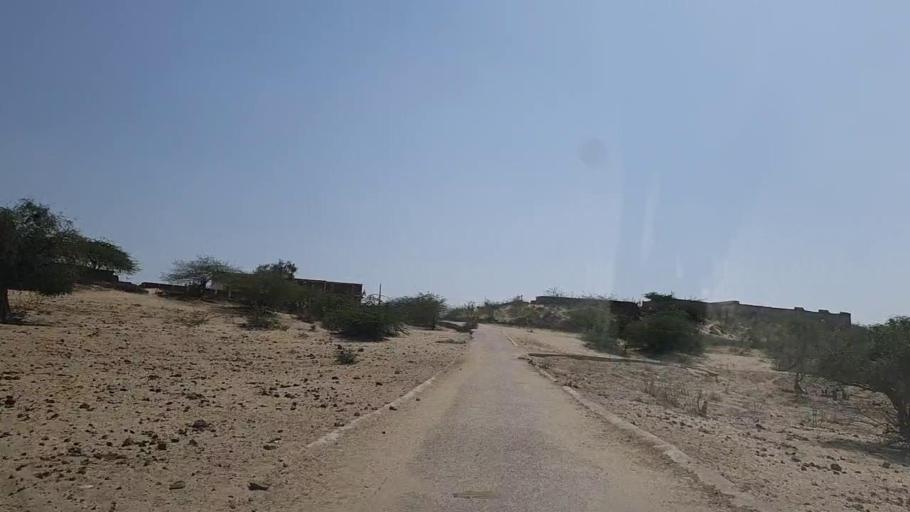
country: PK
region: Sindh
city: Diplo
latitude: 24.5108
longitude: 69.4141
